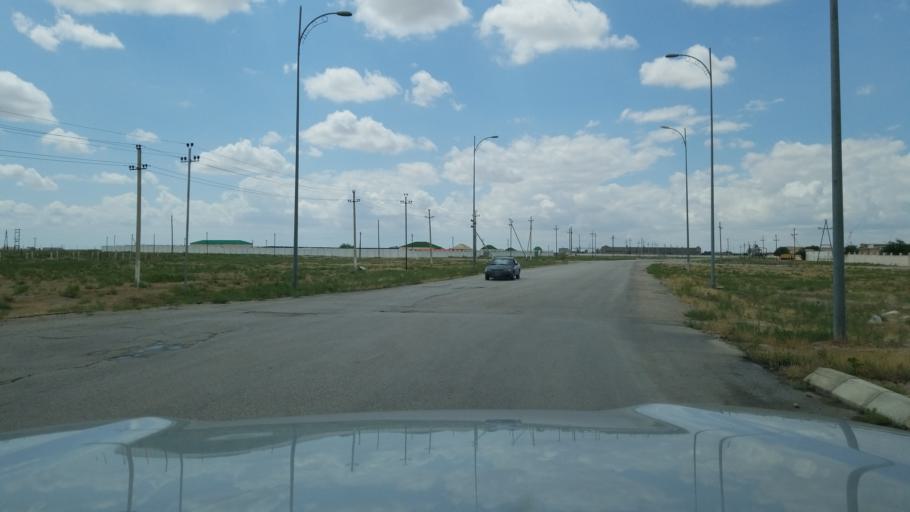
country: TM
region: Balkan
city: Balkanabat
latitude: 39.4865
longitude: 54.3737
